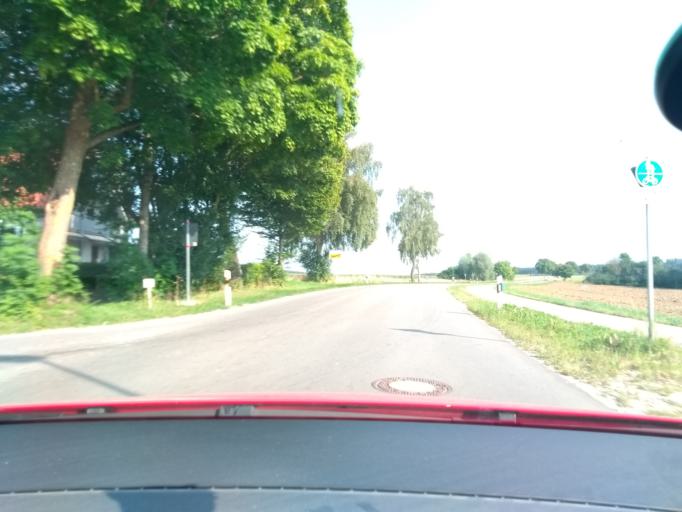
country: DE
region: Bavaria
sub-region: Upper Bavaria
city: Schwabhausen
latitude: 48.4009
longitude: 11.3168
